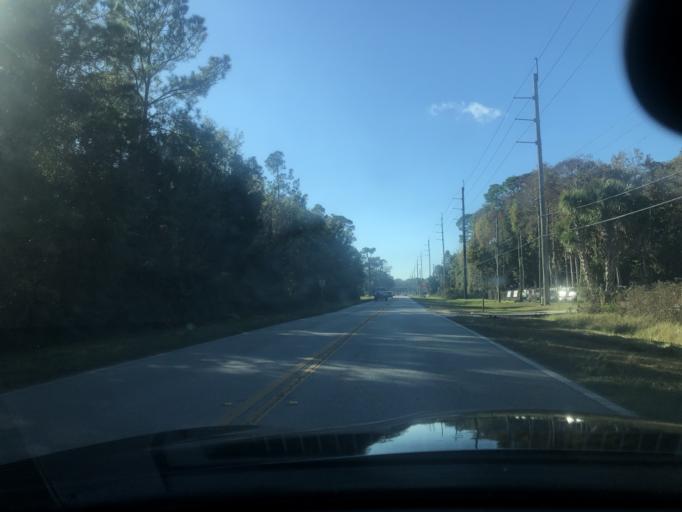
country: US
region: Florida
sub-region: Citrus County
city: Homosassa Springs
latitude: 28.8037
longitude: -82.5714
